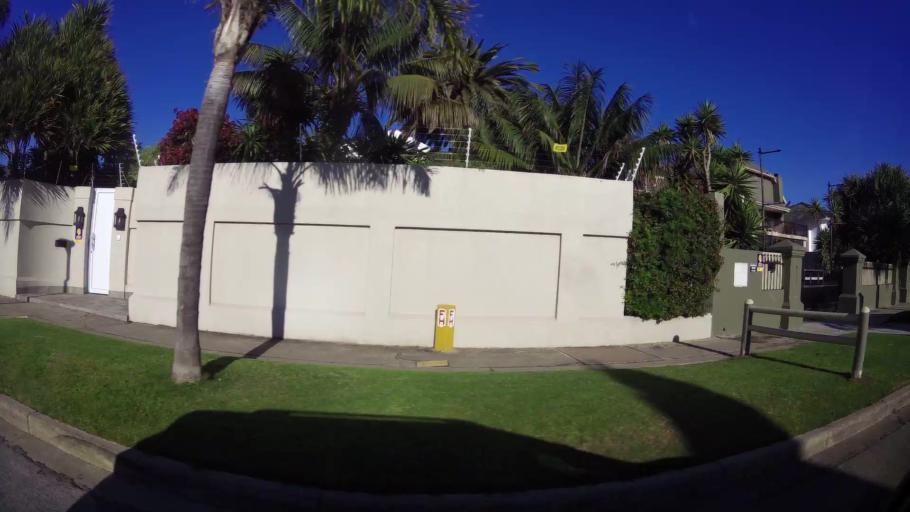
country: ZA
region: Eastern Cape
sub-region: Nelson Mandela Bay Metropolitan Municipality
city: Port Elizabeth
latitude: -33.9849
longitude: 25.6629
